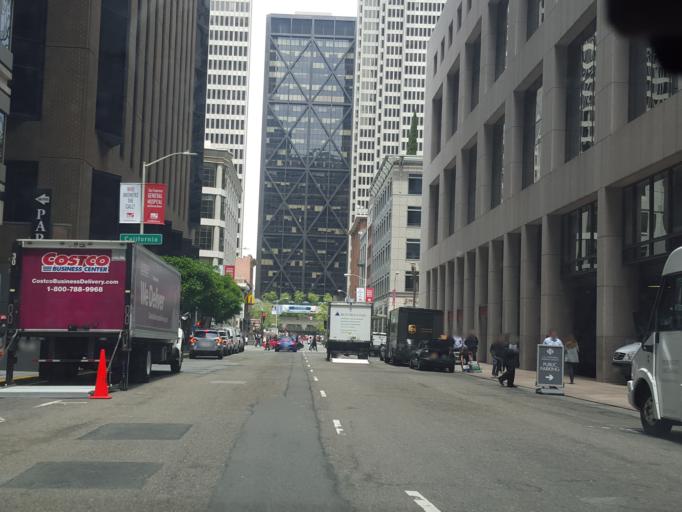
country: US
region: California
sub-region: San Francisco County
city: San Francisco
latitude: 37.7921
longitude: -122.3986
